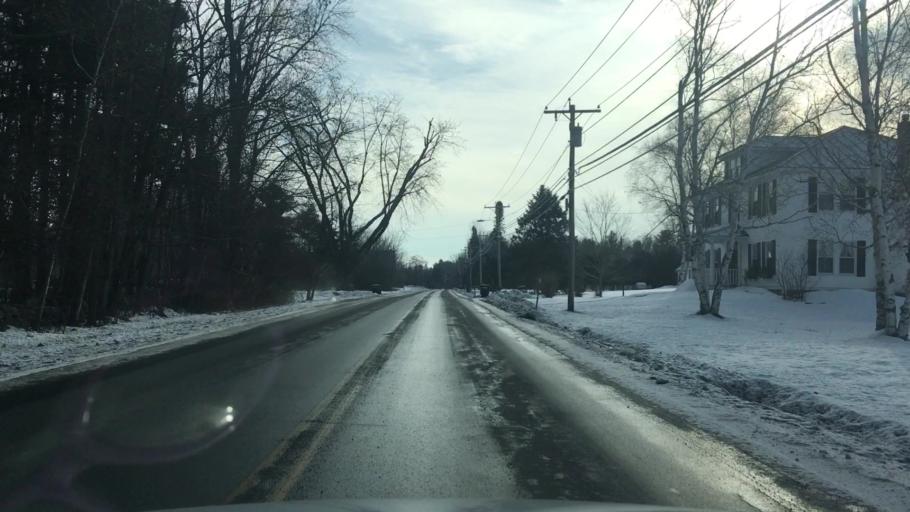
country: US
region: New Hampshire
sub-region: Grafton County
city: Enfield
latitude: 43.6286
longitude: -72.1281
